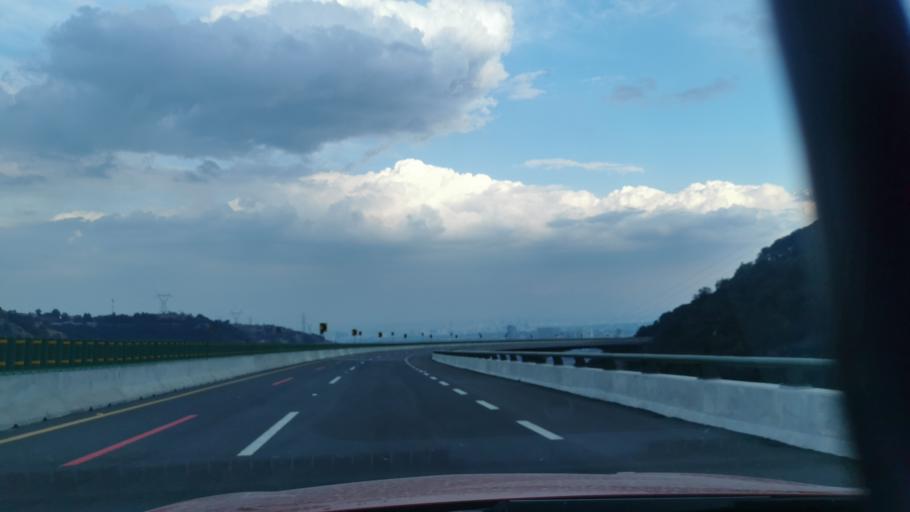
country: MX
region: Mexico
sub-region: Naucalpan de Juarez
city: San Francisco Chimalpa
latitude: 19.4351
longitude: -99.3363
